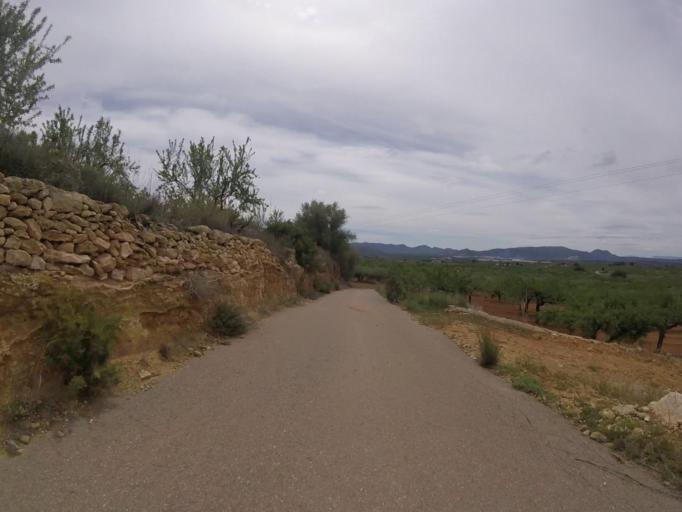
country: ES
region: Valencia
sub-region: Provincia de Castello
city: Benlloch
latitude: 40.1957
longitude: -0.0069
